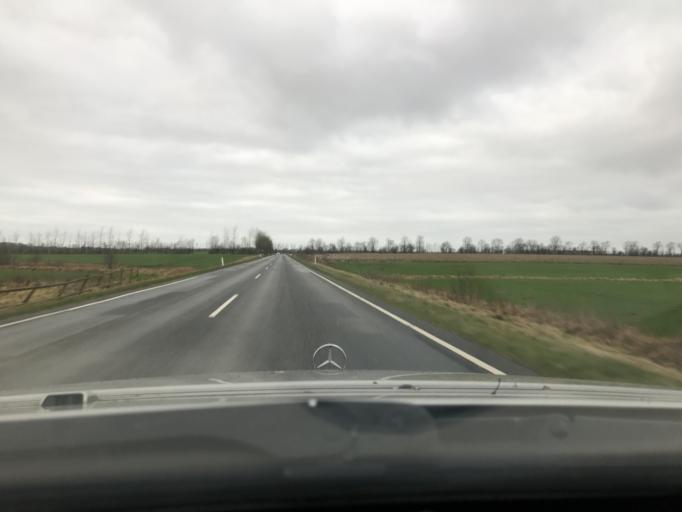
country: DK
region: South Denmark
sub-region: Tonder Kommune
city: Toftlund
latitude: 55.1781
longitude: 9.0141
